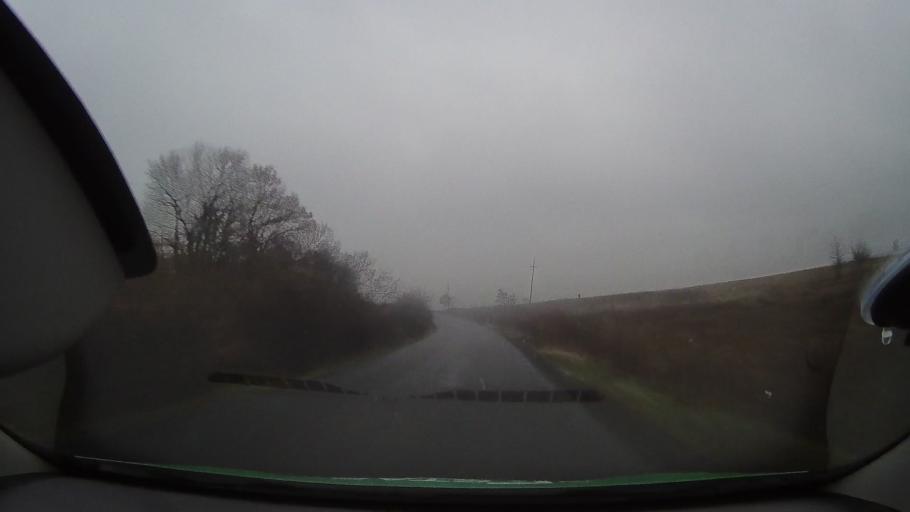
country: RO
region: Bihor
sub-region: Comuna Tinca
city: Gurbediu
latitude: 46.7757
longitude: 21.8809
